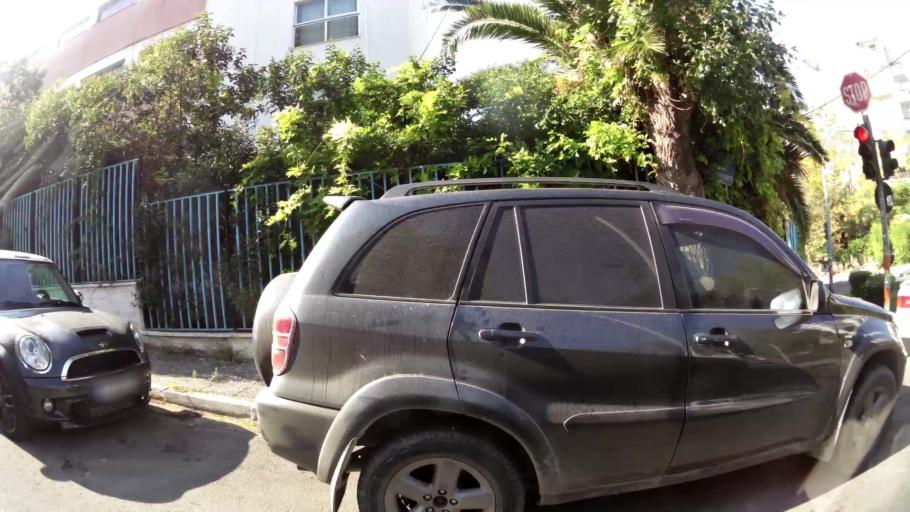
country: GR
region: Attica
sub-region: Nomarchia Athinas
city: Ilioupoli
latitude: 37.9453
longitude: 23.7710
